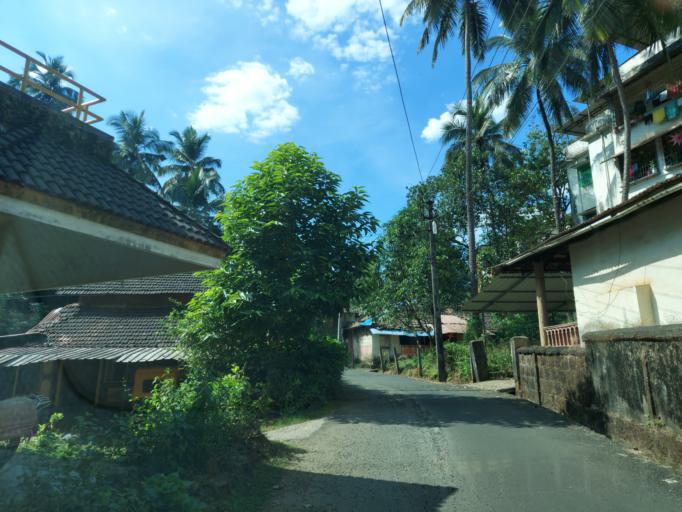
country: IN
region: Maharashtra
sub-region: Sindhudurg
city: Savantvadi
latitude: 15.9039
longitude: 73.8173
